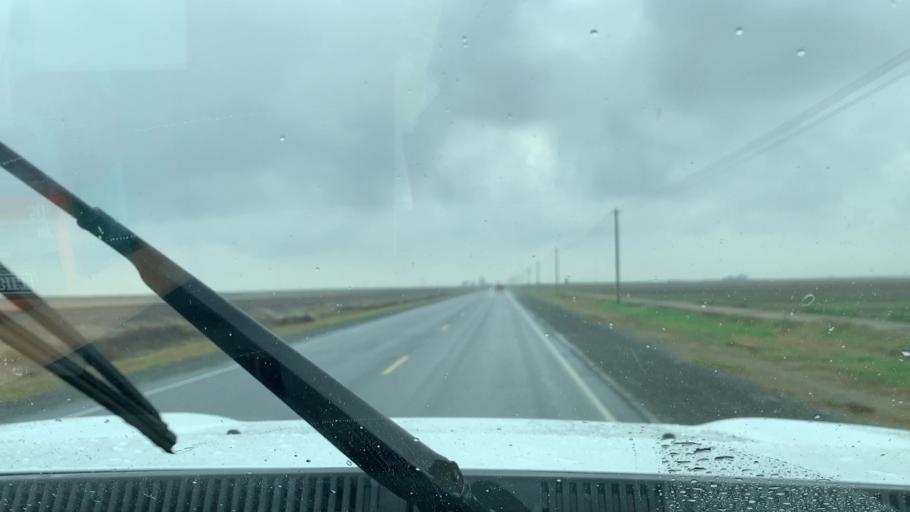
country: US
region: California
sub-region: Tulare County
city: Alpaugh
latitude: 35.9669
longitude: -119.4604
